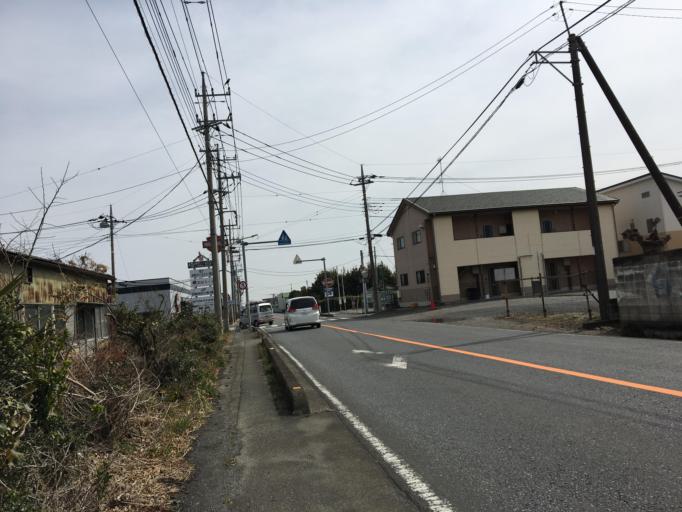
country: JP
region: Saitama
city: Yorii
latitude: 36.1242
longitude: 139.2156
